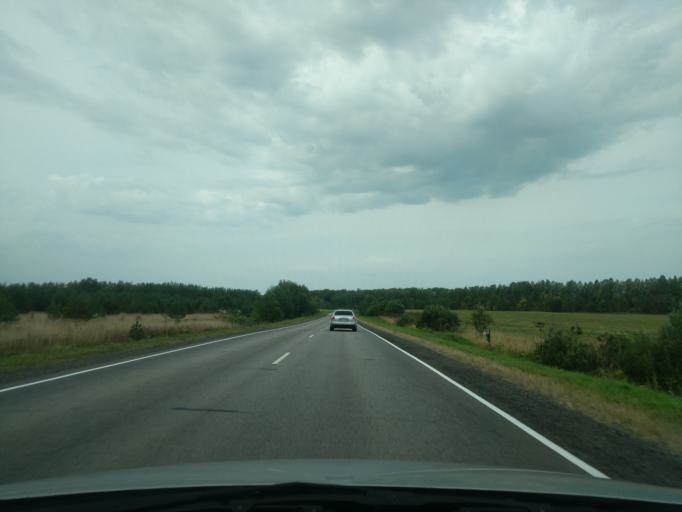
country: RU
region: Kirov
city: Mirnyy
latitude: 58.2736
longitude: 47.7626
